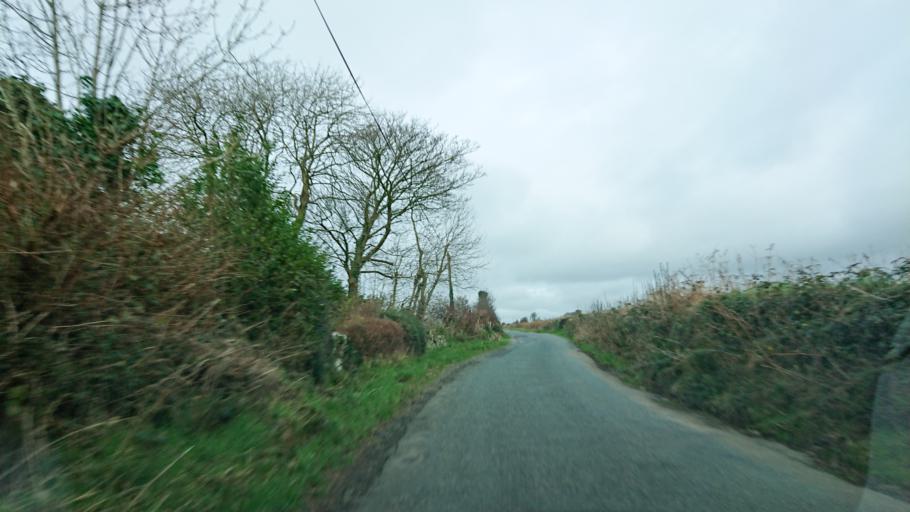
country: IE
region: Munster
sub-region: Waterford
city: Portlaw
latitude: 52.1717
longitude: -7.3059
